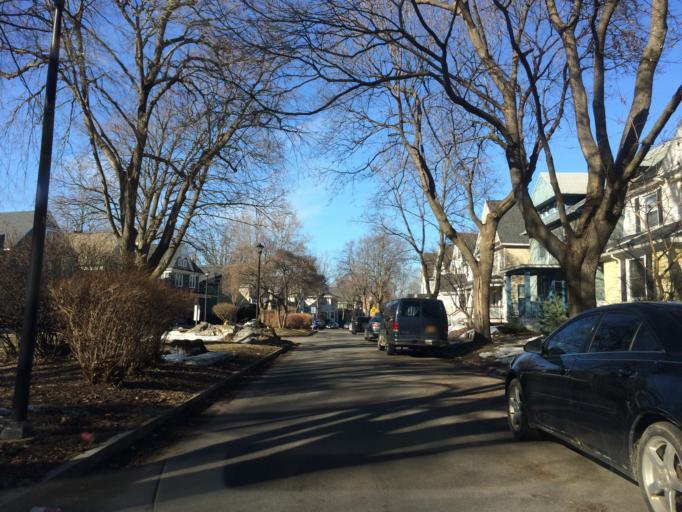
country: US
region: New York
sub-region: Monroe County
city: Rochester
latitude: 43.1425
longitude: -77.5910
